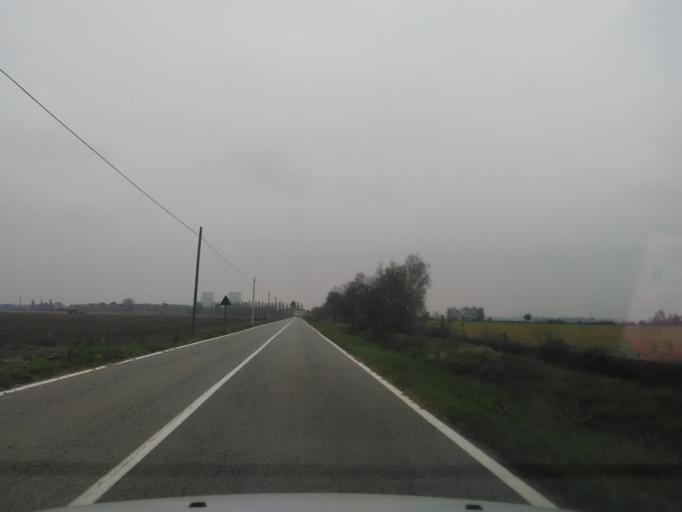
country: IT
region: Piedmont
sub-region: Provincia di Vercelli
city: Bianze
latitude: 45.2576
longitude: 8.1589
